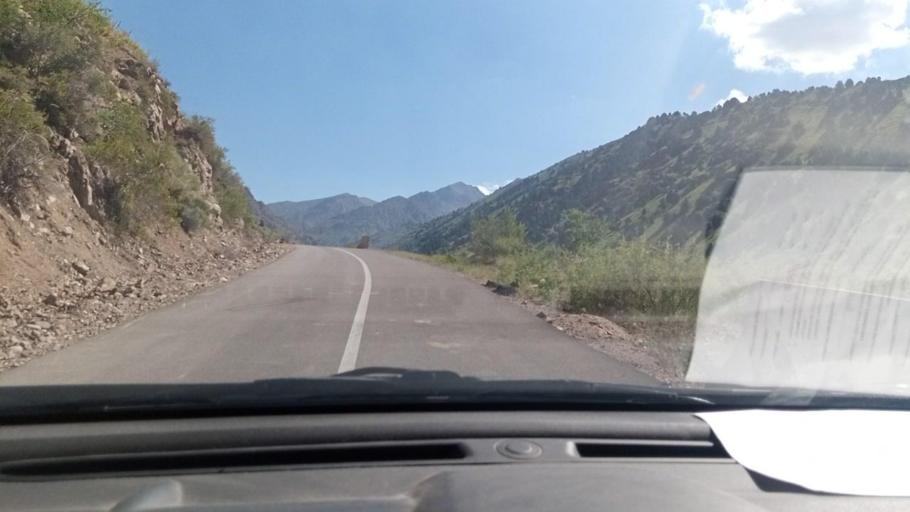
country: UZ
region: Toshkent
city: Yangiobod
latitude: 41.1265
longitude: 70.1079
